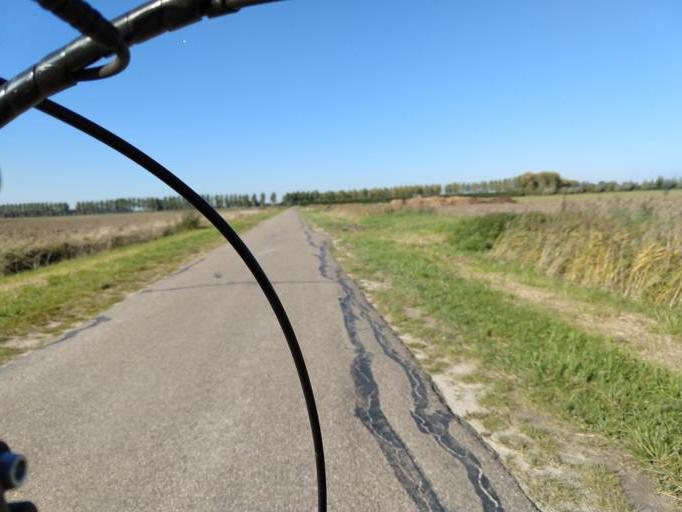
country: NL
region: Zeeland
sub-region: Gemeente Goes
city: Goes
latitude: 51.4423
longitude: 3.8310
